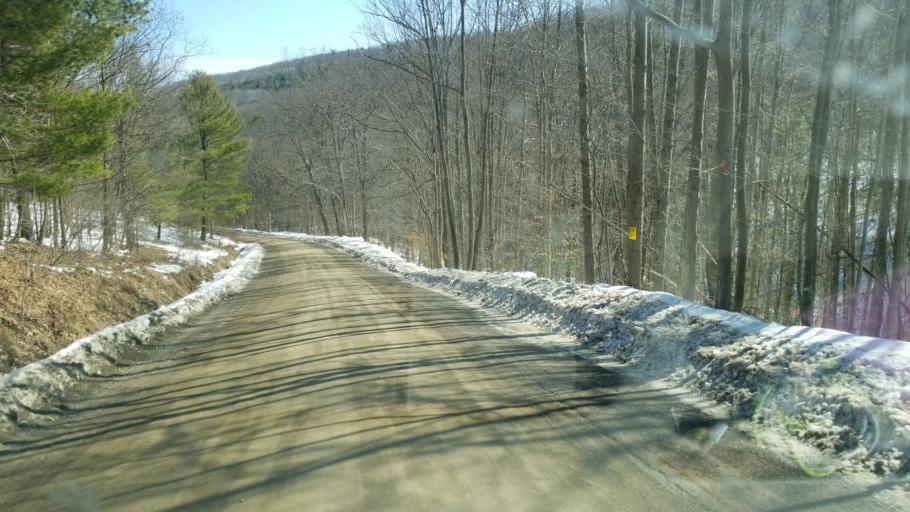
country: US
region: New York
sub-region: Allegany County
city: Alfred
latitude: 42.2464
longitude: -77.7238
